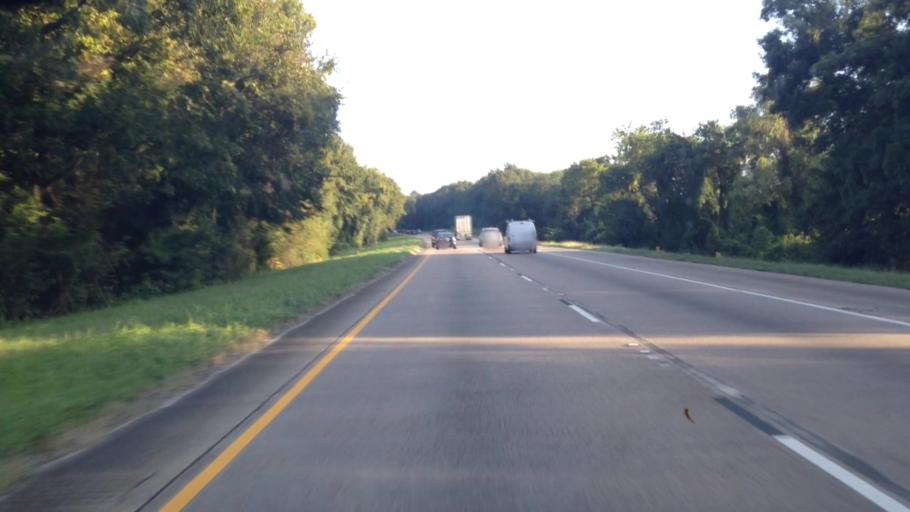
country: US
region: Louisiana
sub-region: Ascension Parish
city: Prairieville
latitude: 30.3046
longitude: -90.9931
